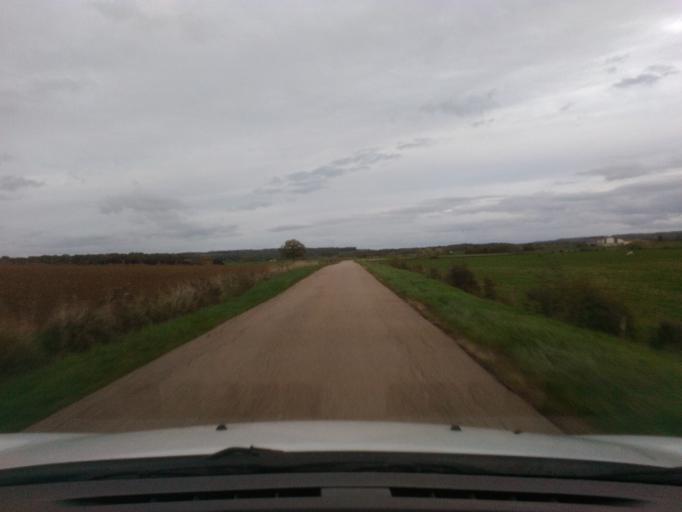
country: FR
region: Lorraine
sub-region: Departement des Vosges
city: Mirecourt
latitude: 48.3364
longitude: 6.0819
